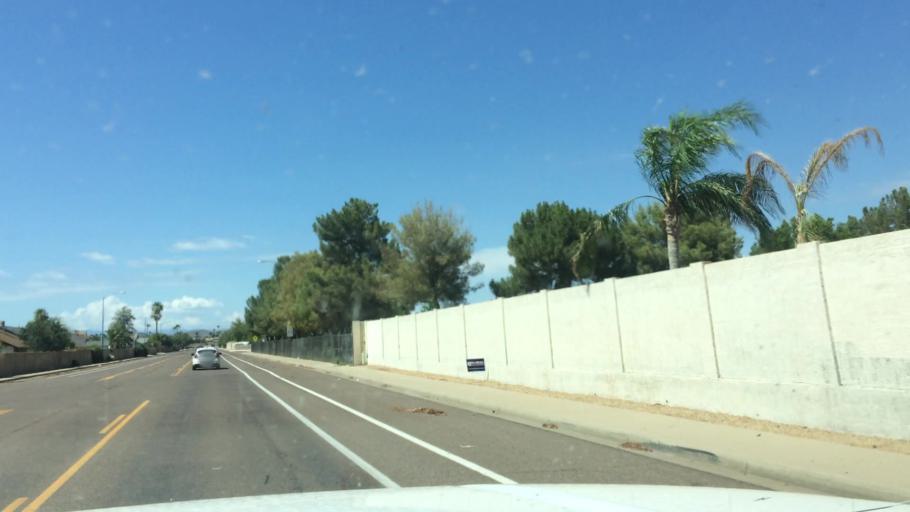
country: US
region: Arizona
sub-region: Maricopa County
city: Sun City
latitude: 33.6466
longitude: -112.2463
